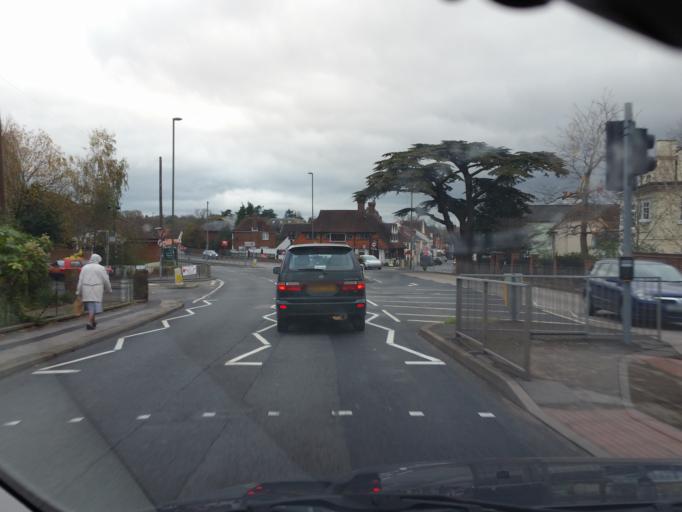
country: GB
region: England
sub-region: Surrey
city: Bagshot
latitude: 51.3598
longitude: -0.6951
